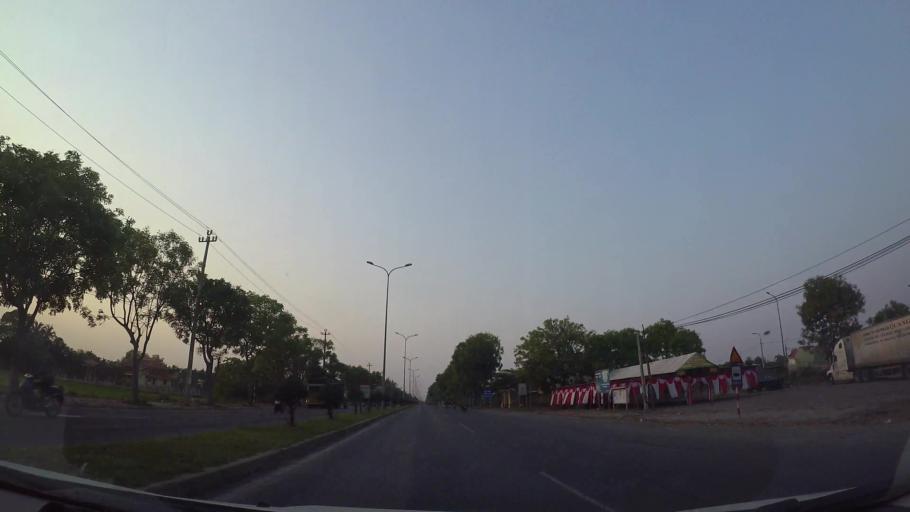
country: VN
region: Da Nang
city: Cam Le
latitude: 15.9530
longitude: 108.2176
